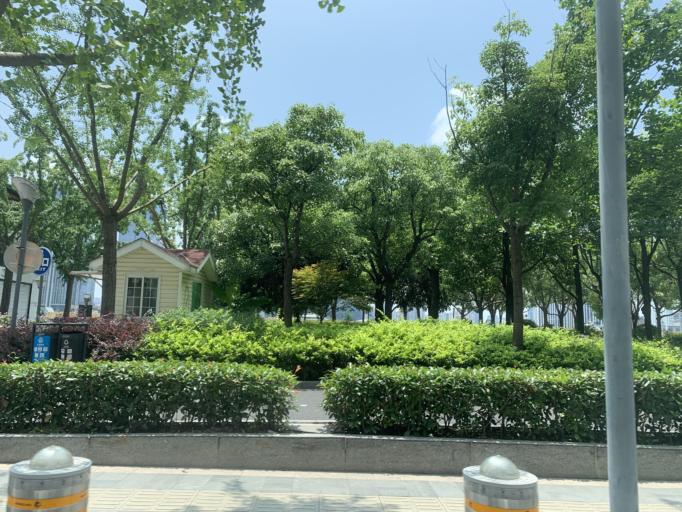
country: CN
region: Shanghai Shi
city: Hongkou
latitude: 31.2345
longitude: 121.4969
